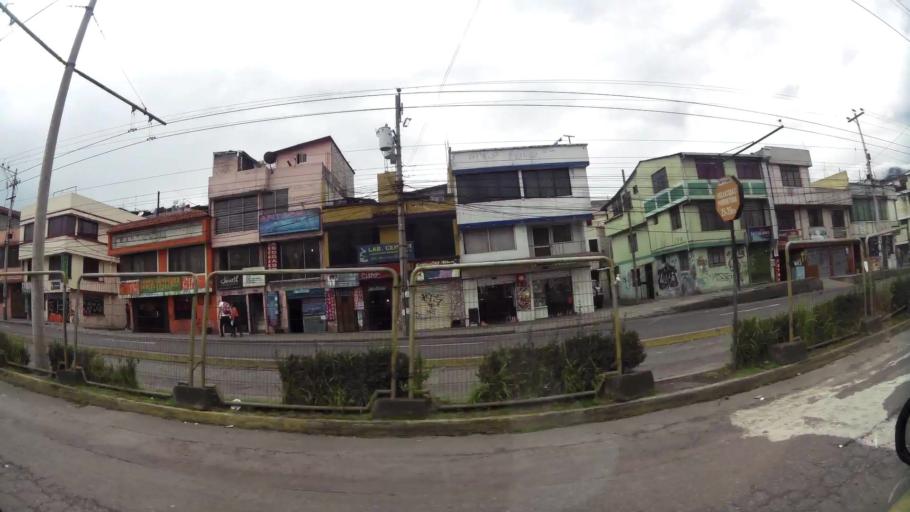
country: EC
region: Pichincha
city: Quito
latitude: -0.2781
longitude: -78.5427
